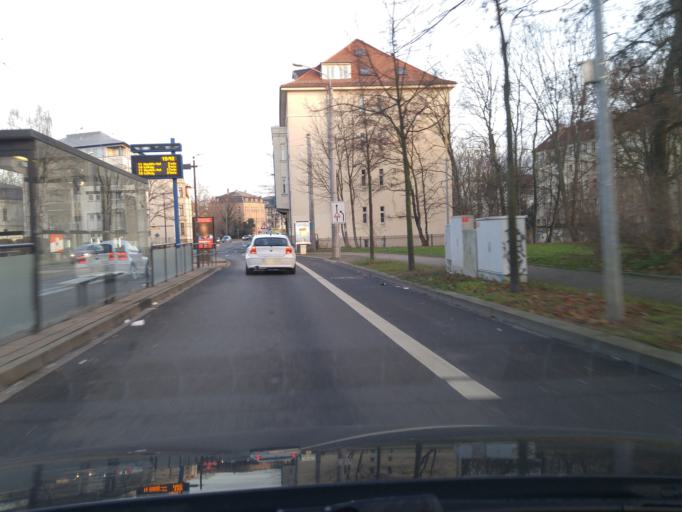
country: DE
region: Saxony
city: Leipzig
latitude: 51.3611
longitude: 12.3712
